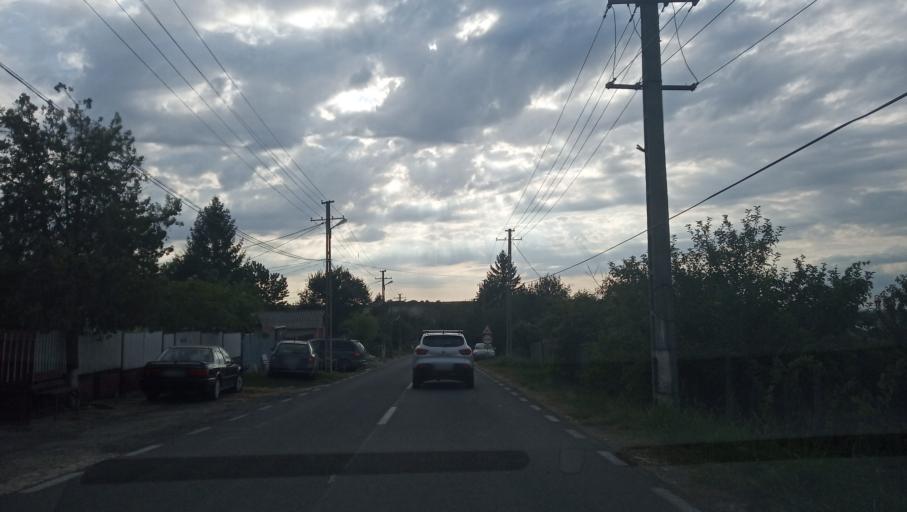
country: RO
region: Constanta
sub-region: Comuna Ostrov
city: Ostrov
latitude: 44.1026
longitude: 27.3722
